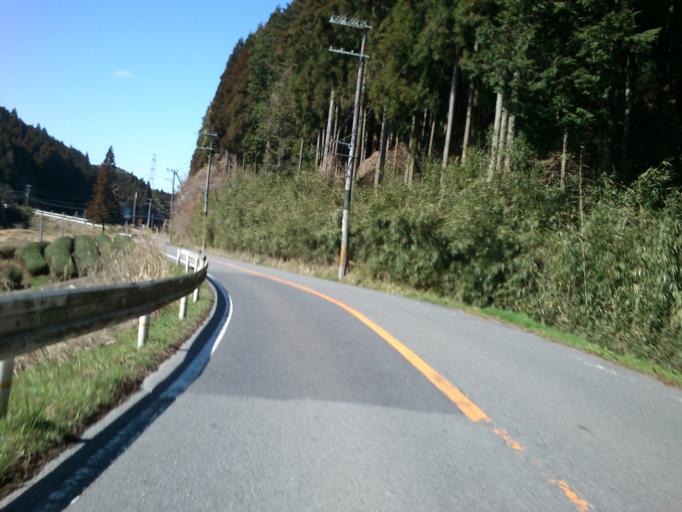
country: JP
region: Kyoto
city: Uji
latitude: 34.8593
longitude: 135.9127
